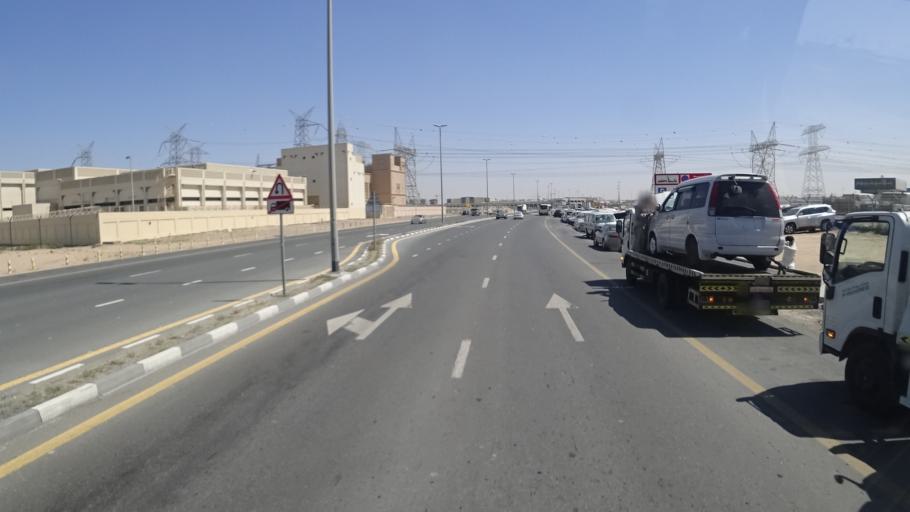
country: AE
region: Ash Shariqah
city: Sharjah
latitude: 25.1744
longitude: 55.3800
